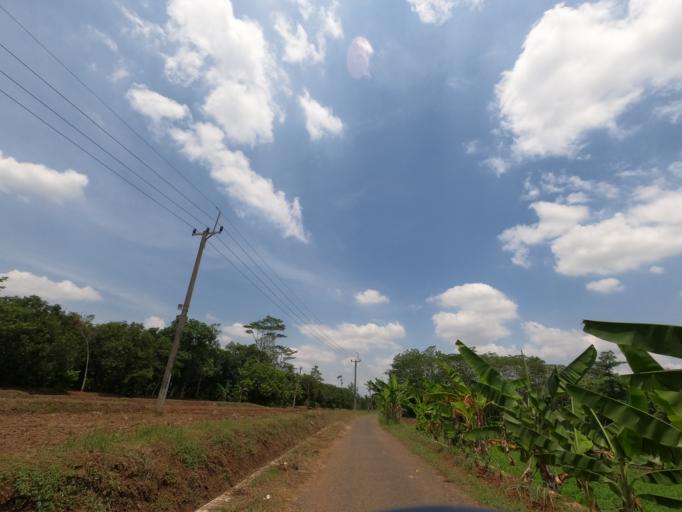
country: ID
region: West Java
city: Pamanukan
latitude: -6.5089
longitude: 107.7704
